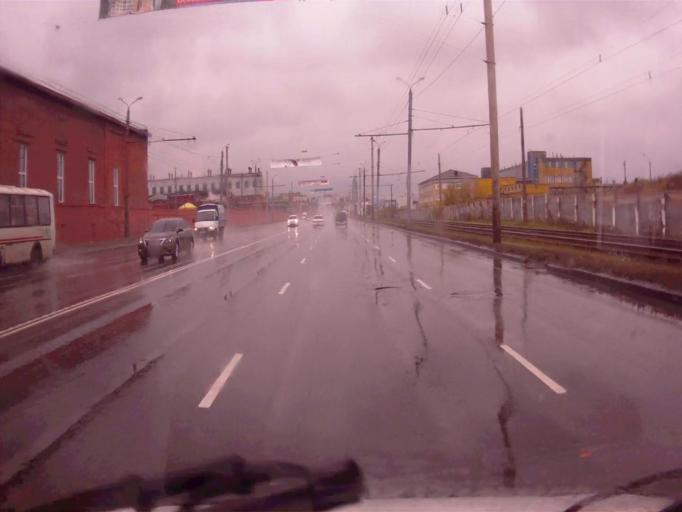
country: RU
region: Chelyabinsk
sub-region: Gorod Chelyabinsk
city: Chelyabinsk
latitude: 55.2089
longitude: 61.3838
